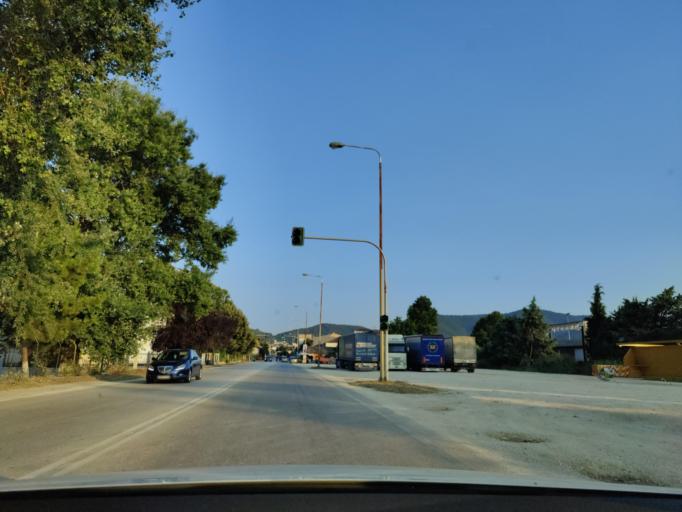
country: GR
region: East Macedonia and Thrace
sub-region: Nomos Kavalas
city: Amygdaleonas
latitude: 40.9671
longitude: 24.3549
